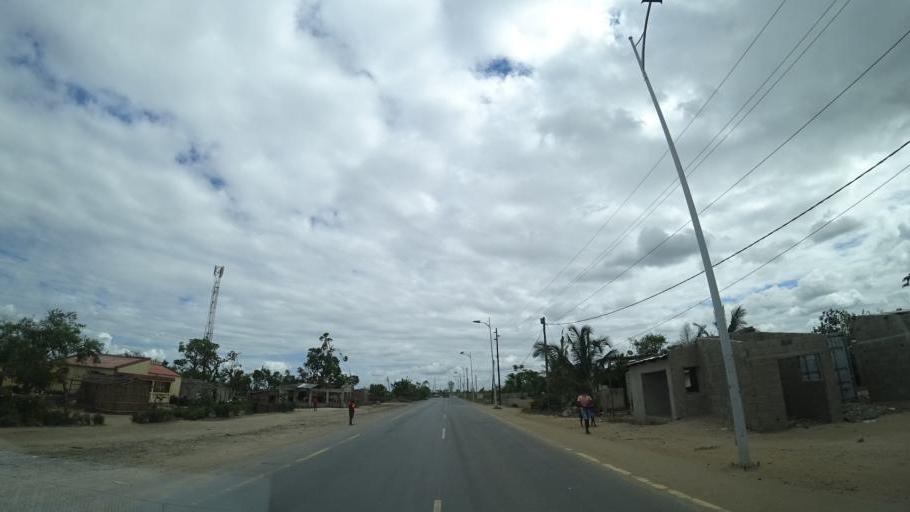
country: MZ
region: Sofala
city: Dondo
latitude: -19.4996
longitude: 34.5960
